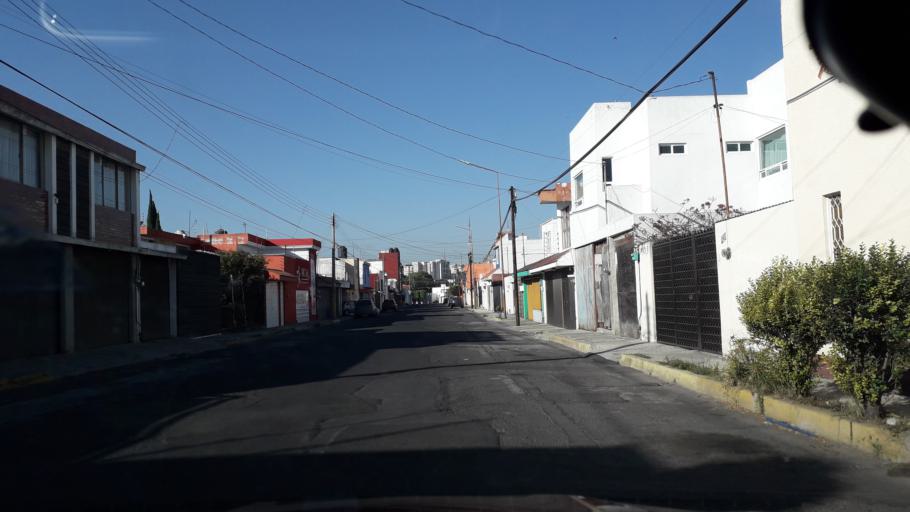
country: MX
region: Puebla
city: Puebla
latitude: 19.0642
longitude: -98.2189
